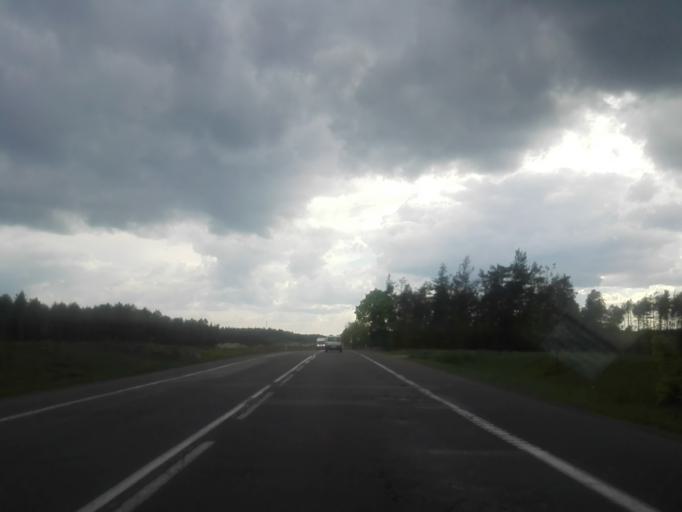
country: PL
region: Podlasie
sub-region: Powiat zambrowski
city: Szumowo
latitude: 52.9027
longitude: 22.0829
